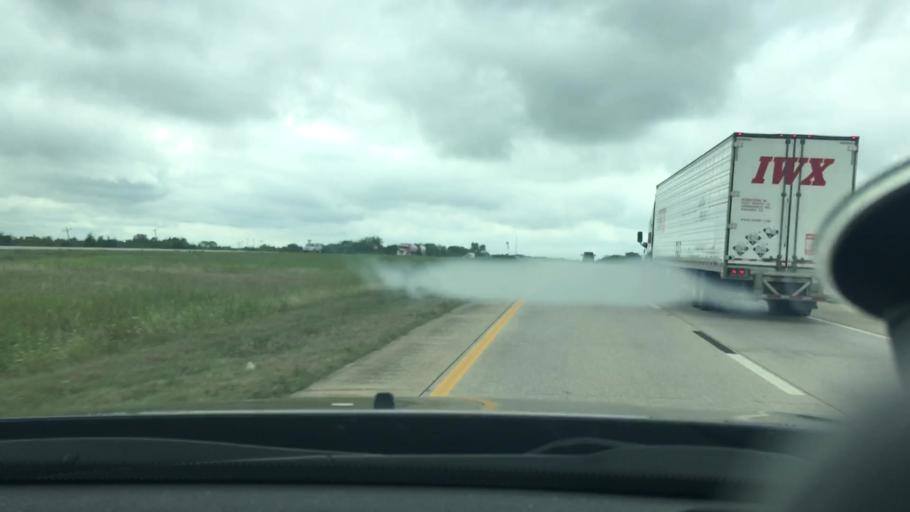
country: US
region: Oklahoma
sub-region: Bryan County
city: Durant
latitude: 34.1656
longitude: -96.2557
